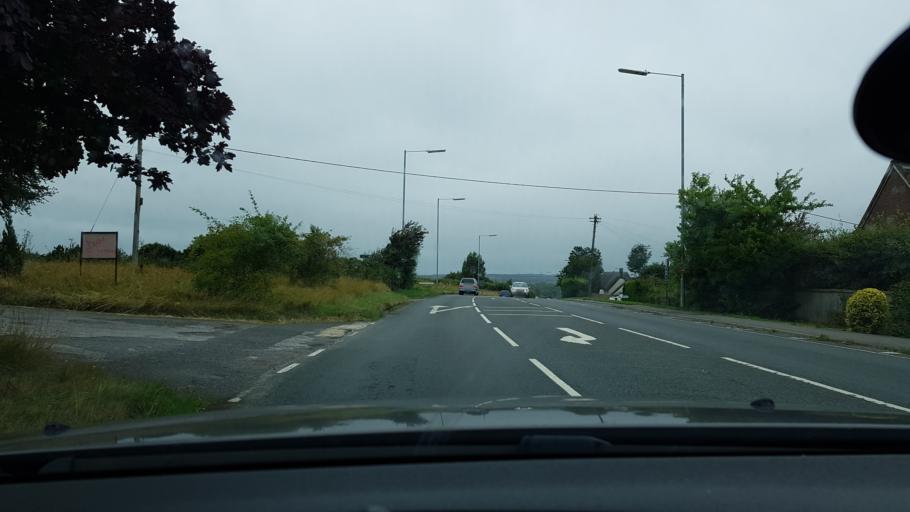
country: GB
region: England
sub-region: Wiltshire
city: Calne
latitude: 51.4286
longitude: -1.9545
